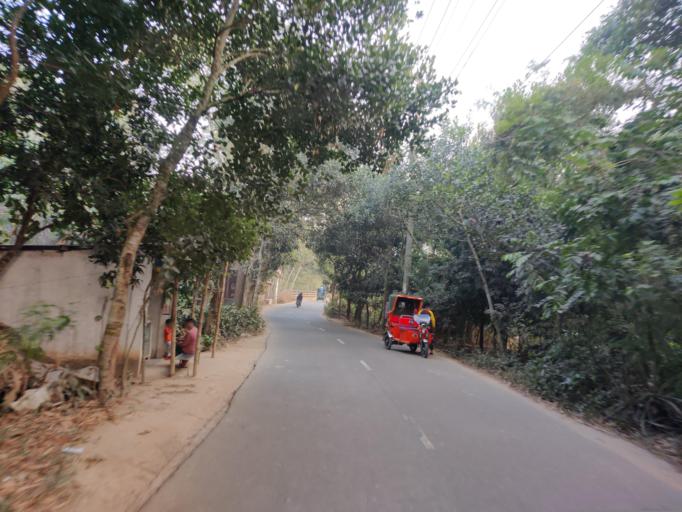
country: BD
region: Dhaka
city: Bajitpur
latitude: 24.1570
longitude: 90.7684
